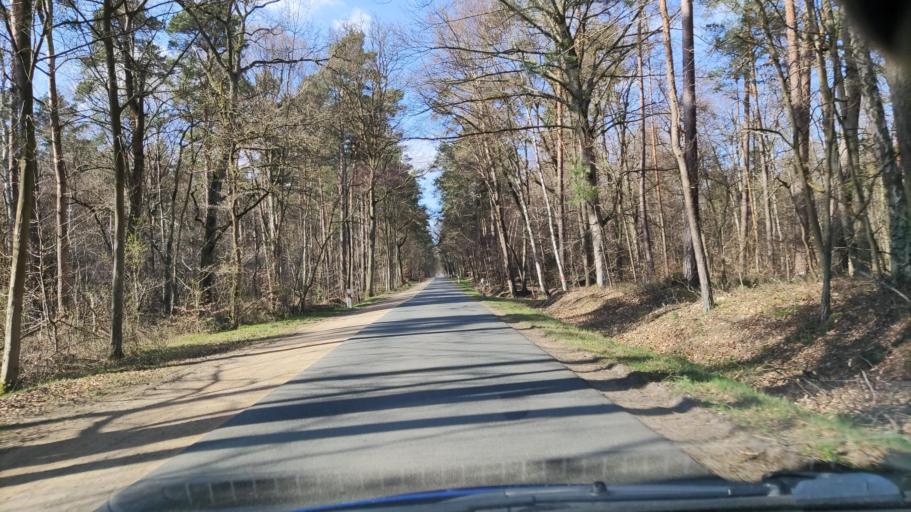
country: DE
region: Lower Saxony
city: Langendorf
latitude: 53.0402
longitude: 11.2498
